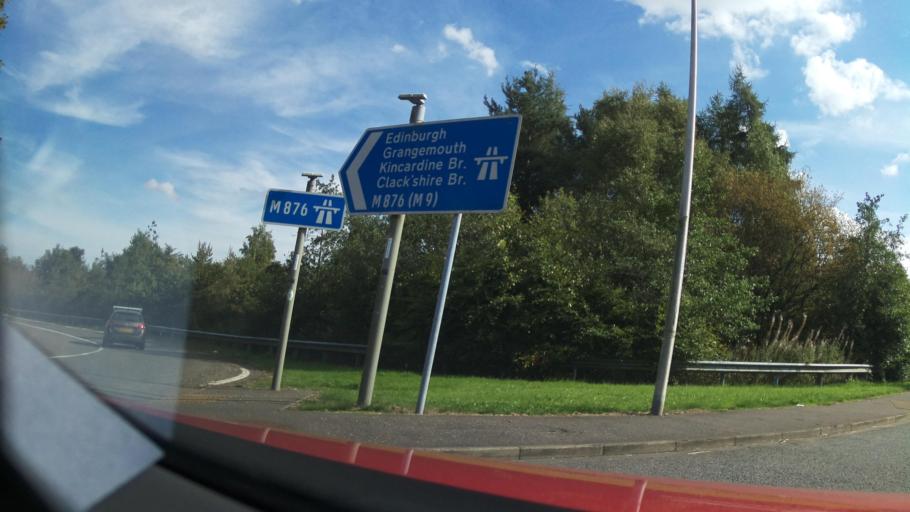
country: GB
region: Scotland
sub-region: Falkirk
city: Larbert
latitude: 56.0331
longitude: -3.8512
